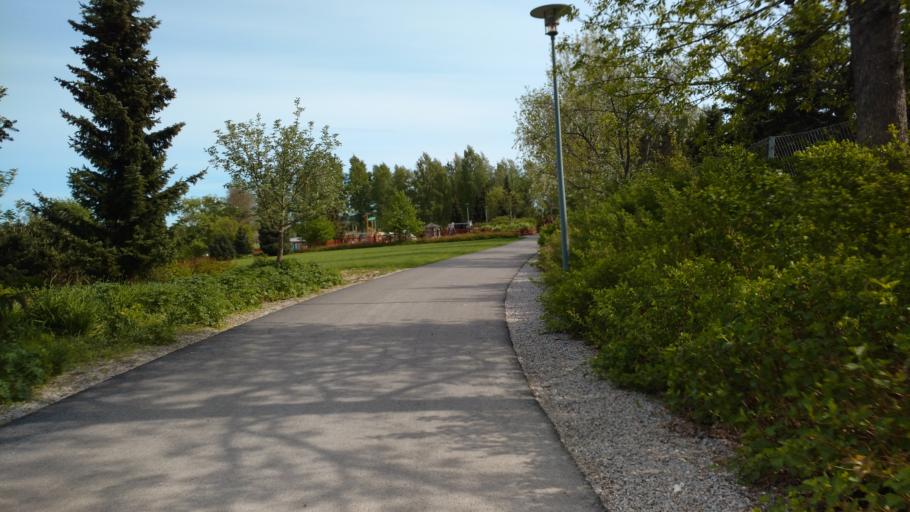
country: FI
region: Varsinais-Suomi
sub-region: Salo
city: Salo
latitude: 60.3817
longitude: 23.1450
